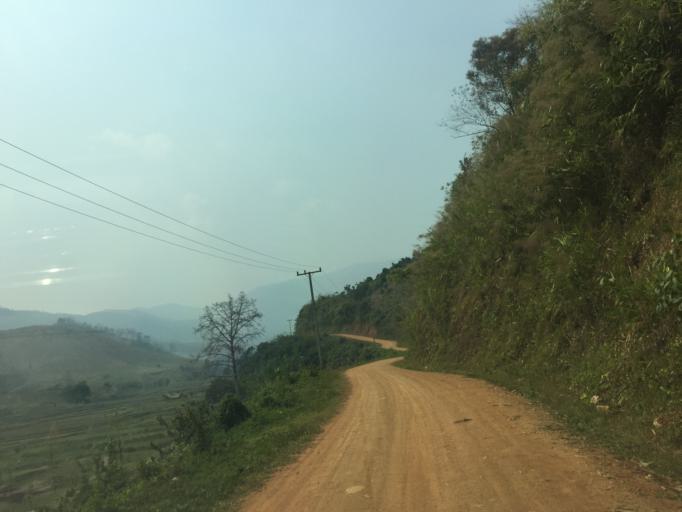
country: TH
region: Phayao
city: Phu Sang
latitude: 19.5807
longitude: 100.5280
